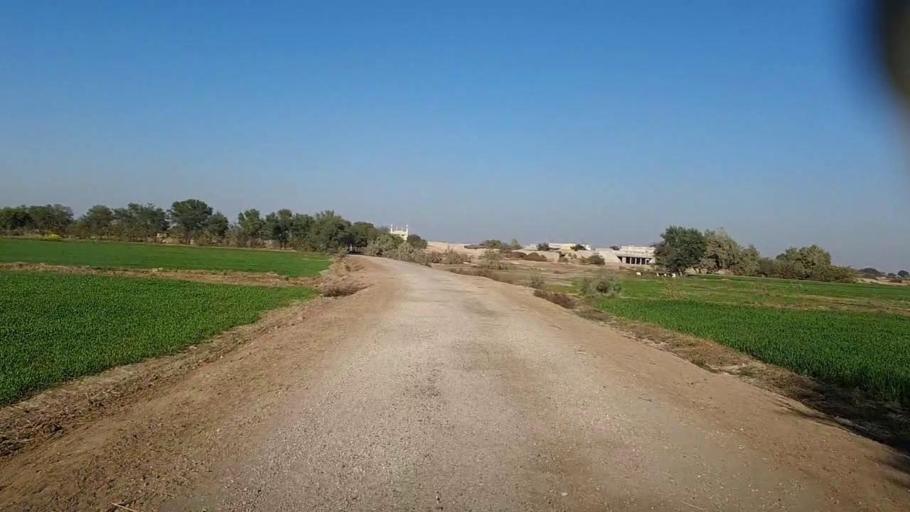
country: PK
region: Sindh
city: Khairpur
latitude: 27.8915
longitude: 69.7525
